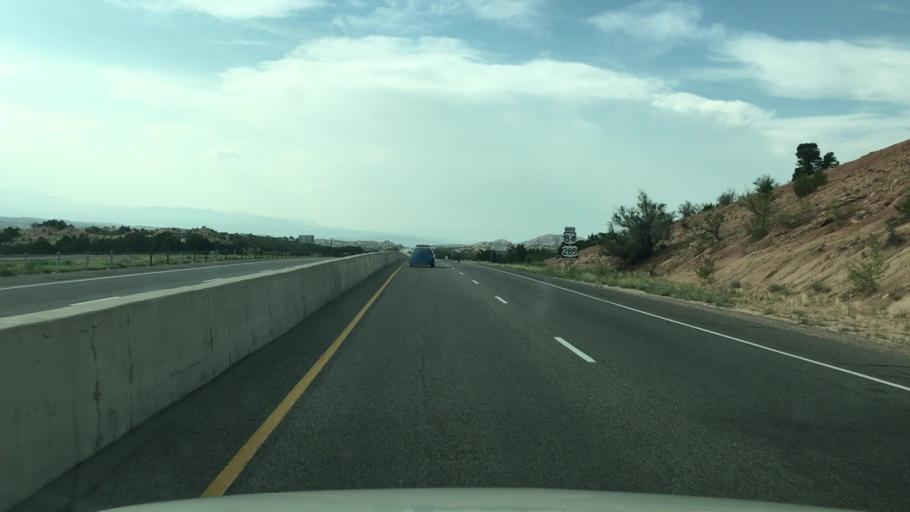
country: US
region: New Mexico
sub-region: Santa Fe County
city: Santa Fe
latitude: 35.7902
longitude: -105.9521
